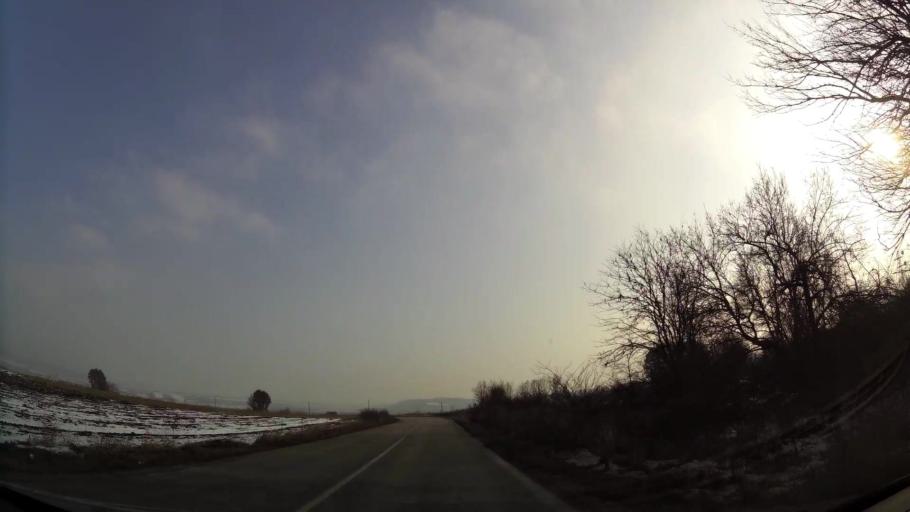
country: MK
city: Miladinovci
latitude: 41.9741
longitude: 21.6322
